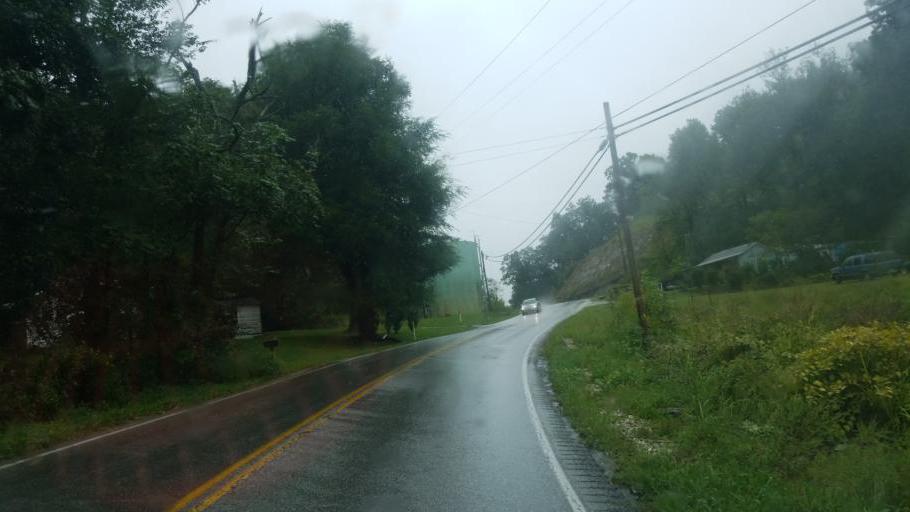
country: US
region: Kentucky
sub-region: Greenup County
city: South Shore
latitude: 38.7127
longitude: -82.9546
